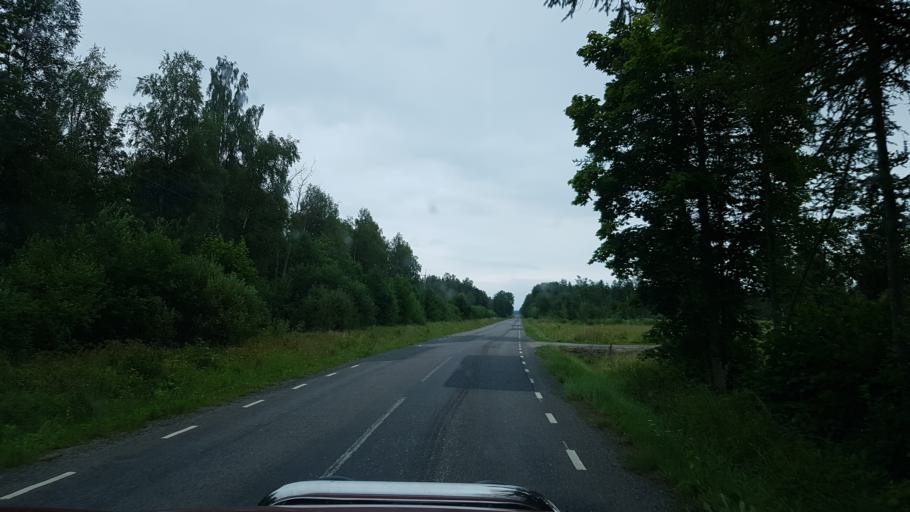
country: EE
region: Ida-Virumaa
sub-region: Johvi vald
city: Johvi
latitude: 59.4141
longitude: 27.4120
